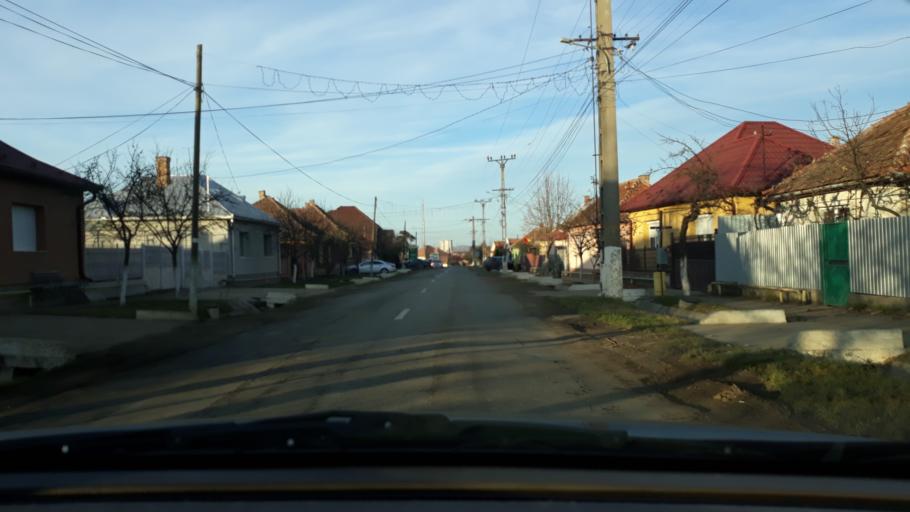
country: RO
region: Bihor
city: Foglas
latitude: 47.2503
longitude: 22.5330
